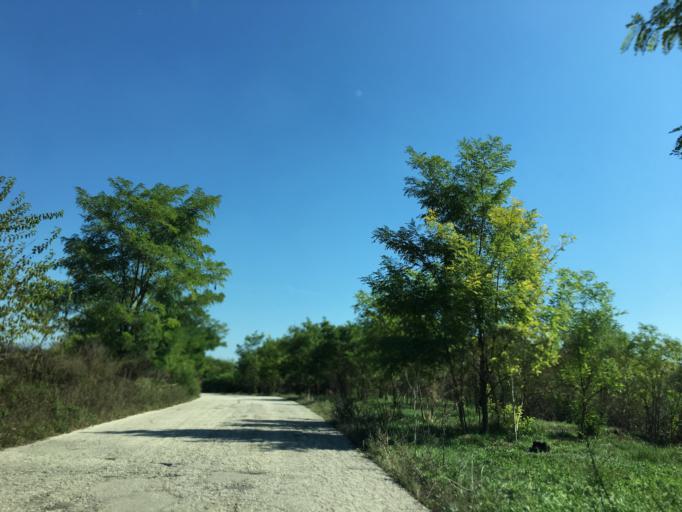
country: BG
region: Pleven
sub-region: Obshtina Knezha
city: Knezha
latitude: 43.5430
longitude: 24.1515
